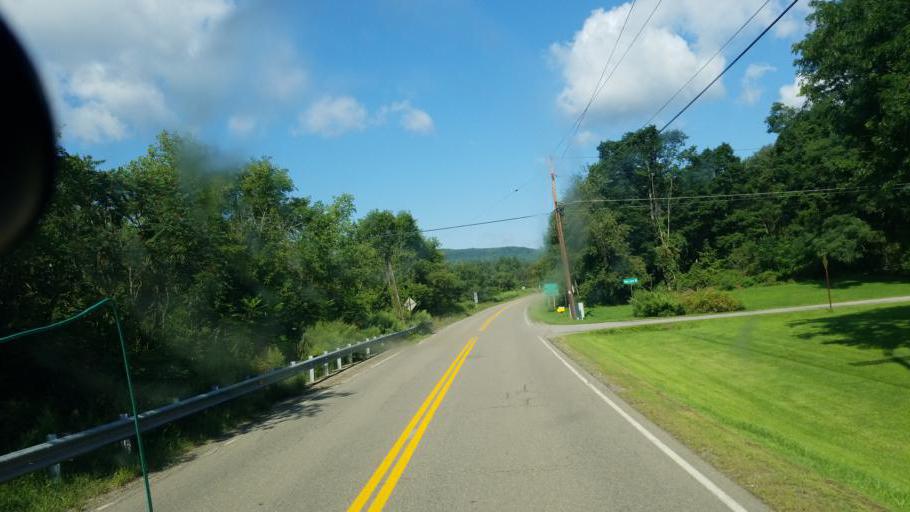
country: US
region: New York
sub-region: Steuben County
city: Canisteo
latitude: 42.2654
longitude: -77.5786
